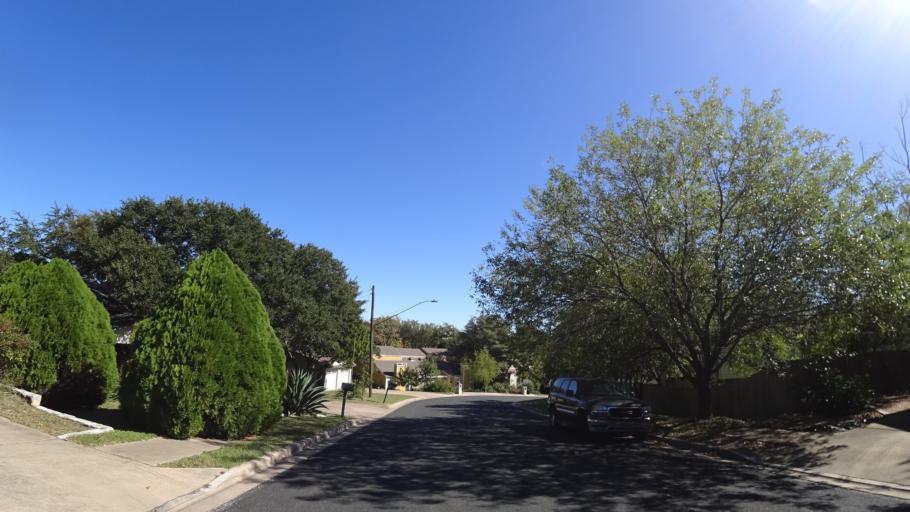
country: US
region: Texas
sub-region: Travis County
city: Rollingwood
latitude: 30.2346
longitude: -97.7796
